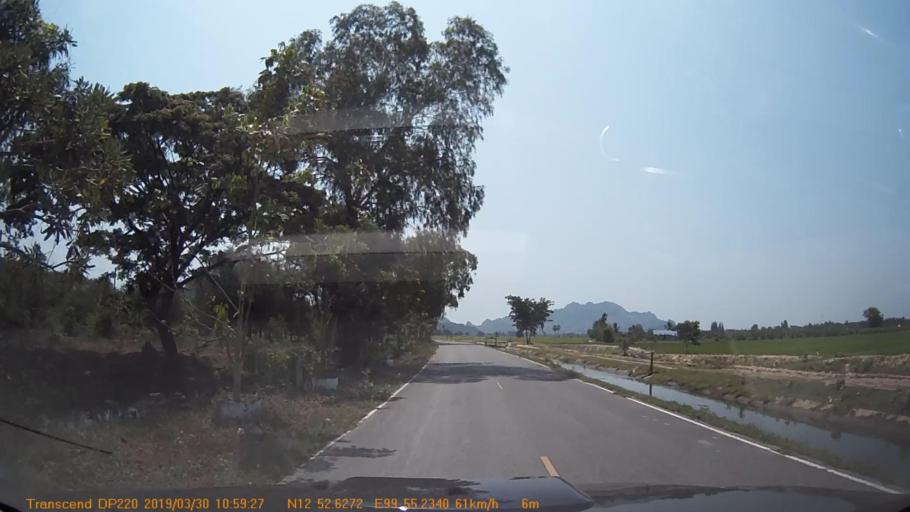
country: TH
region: Phetchaburi
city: Tha Yang
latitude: 12.8769
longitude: 99.9208
